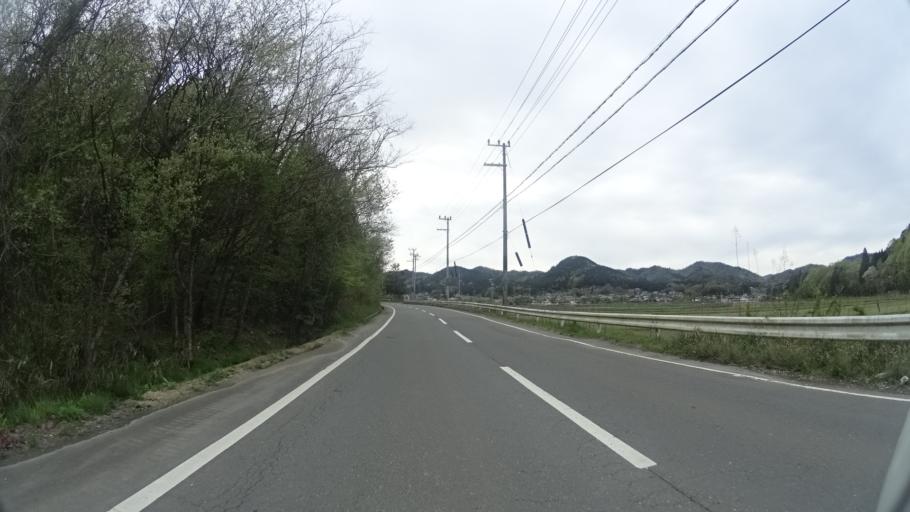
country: JP
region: Kyoto
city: Ayabe
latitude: 35.1855
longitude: 135.4246
